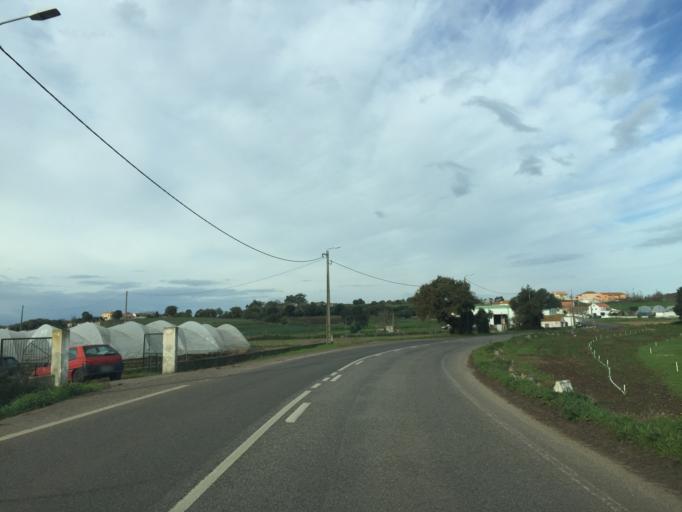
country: PT
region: Lisbon
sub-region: Sintra
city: Almargem
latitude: 38.8643
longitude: -9.2815
